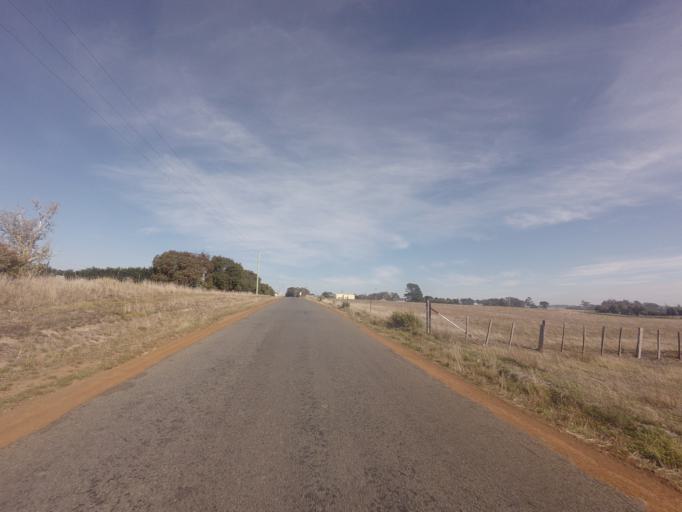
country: AU
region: Tasmania
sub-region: Sorell
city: Sorell
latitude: -42.4515
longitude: 147.4618
